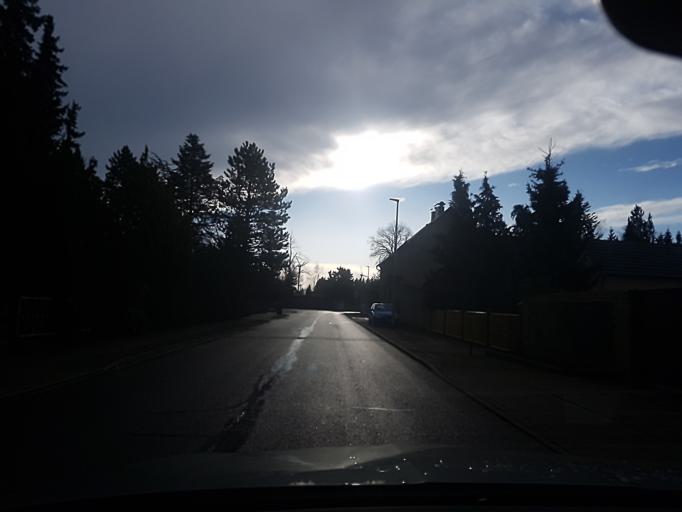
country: DE
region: Brandenburg
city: Falkenberg
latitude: 51.5935
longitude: 13.2949
